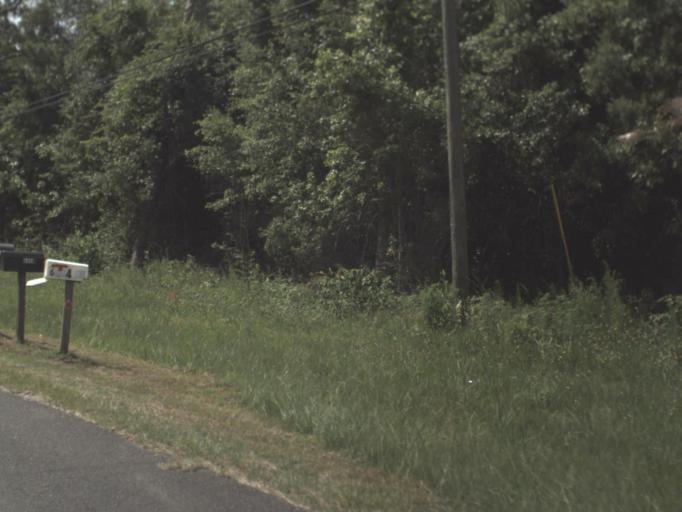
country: US
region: Florida
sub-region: Clay County
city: Green Cove Springs
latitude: 29.9871
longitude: -81.5708
